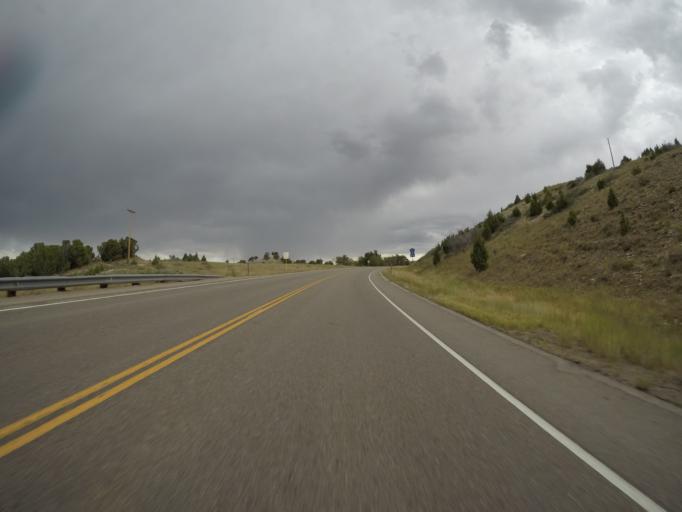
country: US
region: Colorado
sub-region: Rio Blanco County
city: Rangely
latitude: 40.3540
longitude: -108.4512
